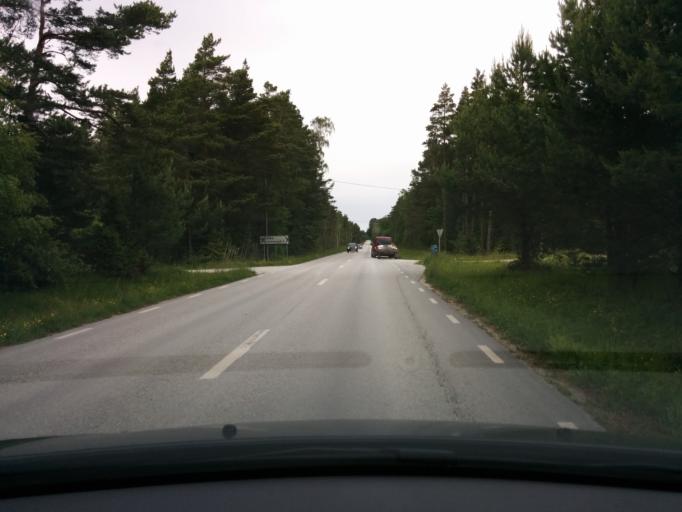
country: SE
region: Gotland
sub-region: Gotland
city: Slite
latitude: 57.6386
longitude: 18.7652
